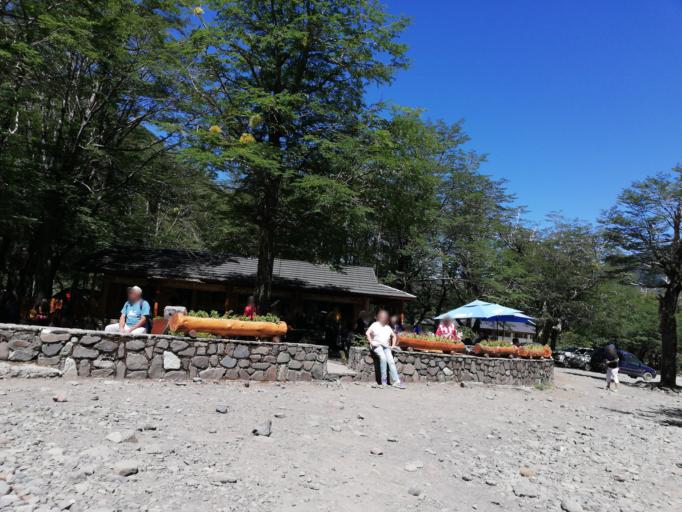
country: AR
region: Neuquen
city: Villa La Angostura
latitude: -41.1940
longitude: -71.8320
